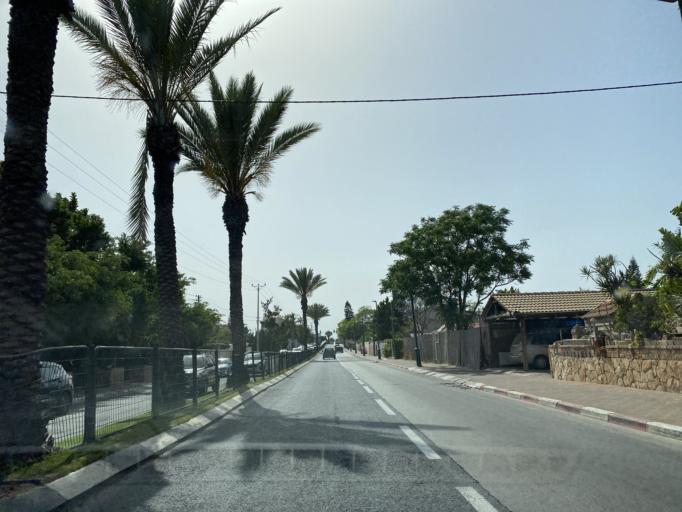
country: IL
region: Tel Aviv
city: Herzliyya
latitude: 32.1764
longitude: 34.8484
